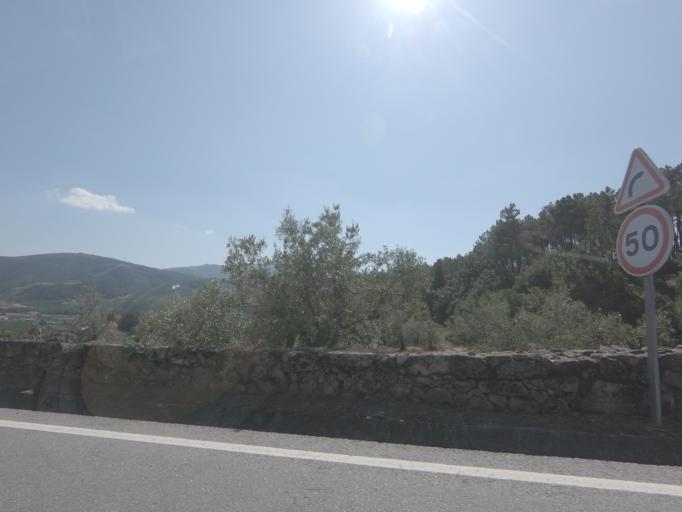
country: PT
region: Viseu
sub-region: Tarouca
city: Tarouca
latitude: 41.0265
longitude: -7.7456
